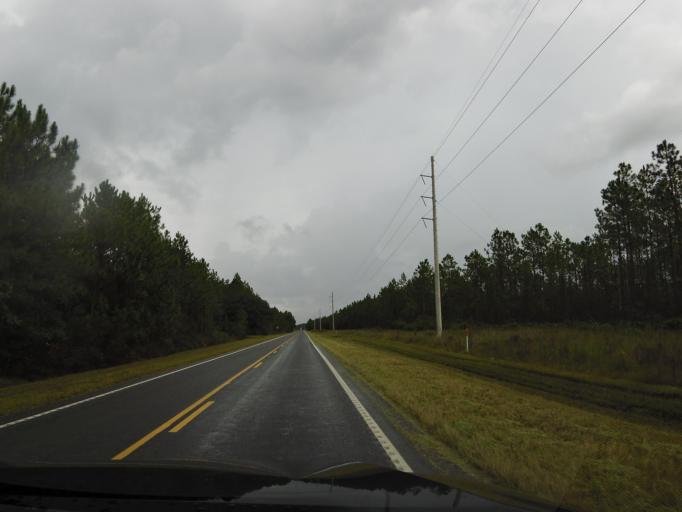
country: US
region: Florida
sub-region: Duval County
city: Baldwin
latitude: 30.4874
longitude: -82.0408
